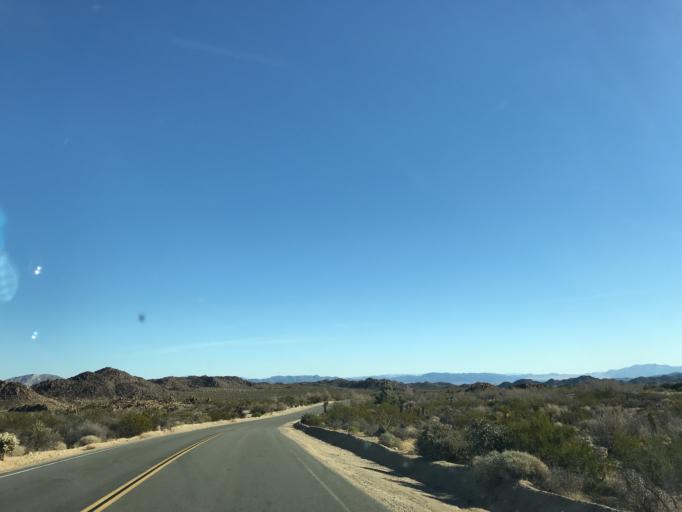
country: US
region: California
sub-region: Riverside County
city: Mecca
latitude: 33.7907
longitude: -115.7914
